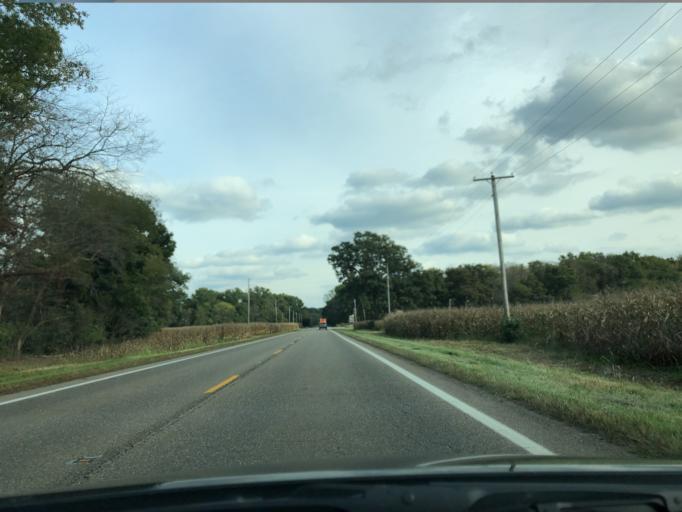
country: US
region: Ohio
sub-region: Stark County
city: Beach City
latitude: 40.6382
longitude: -81.5716
